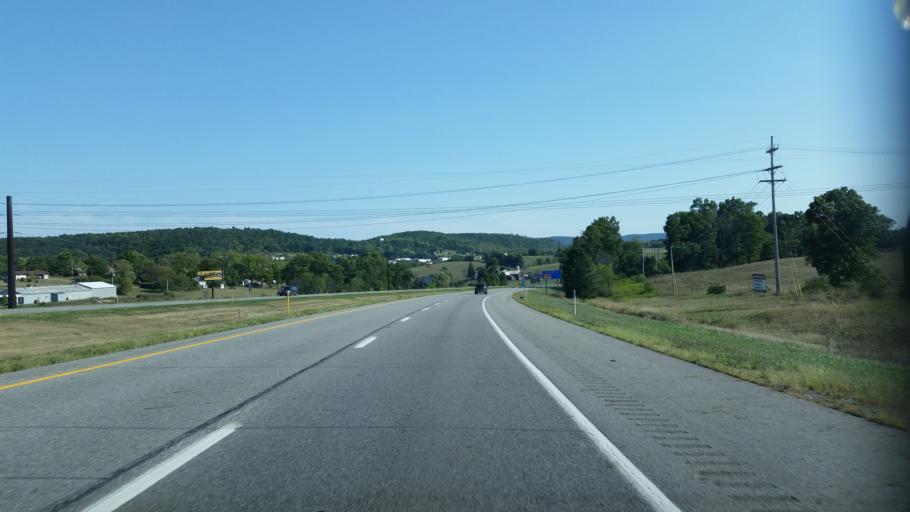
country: US
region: Pennsylvania
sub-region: Bedford County
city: Bedford
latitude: 40.0713
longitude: -78.5199
